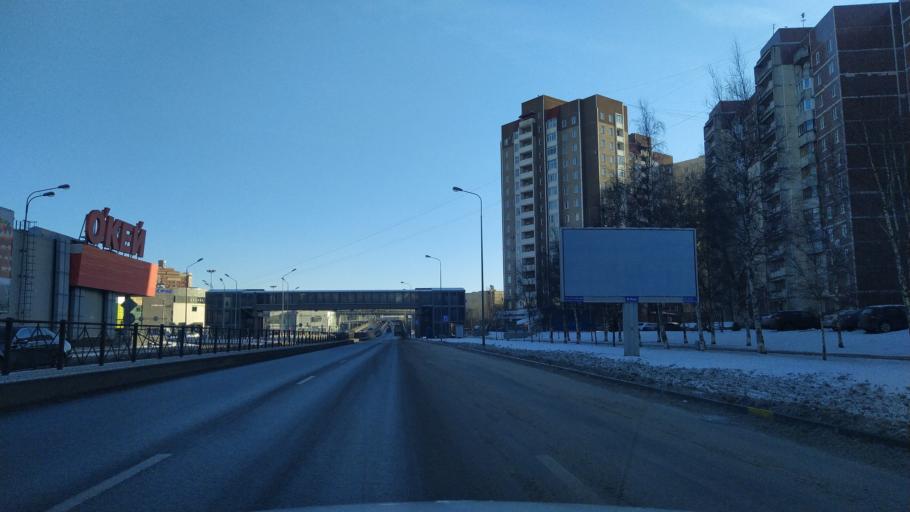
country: RU
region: St.-Petersburg
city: Staraya Derevnya
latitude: 59.9887
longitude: 30.2238
